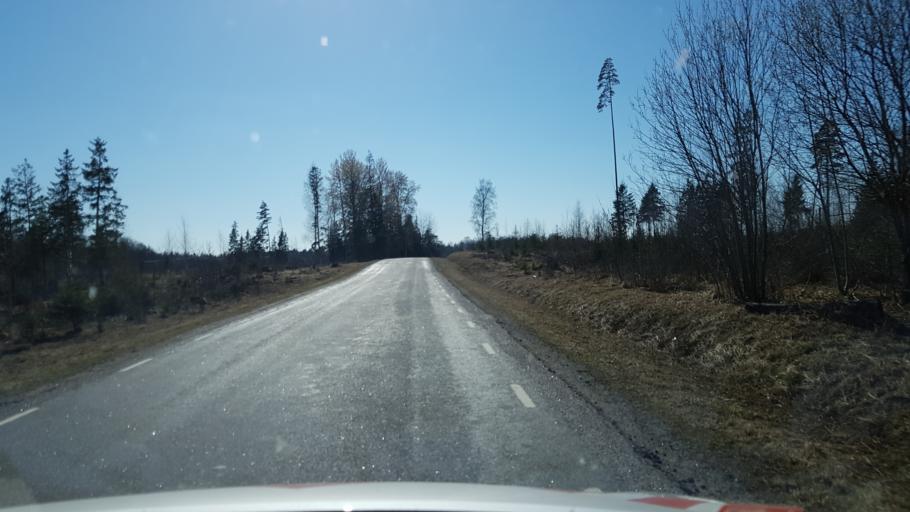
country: EE
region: Laeaene-Virumaa
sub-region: Tamsalu vald
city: Tamsalu
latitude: 59.0757
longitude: 26.1361
